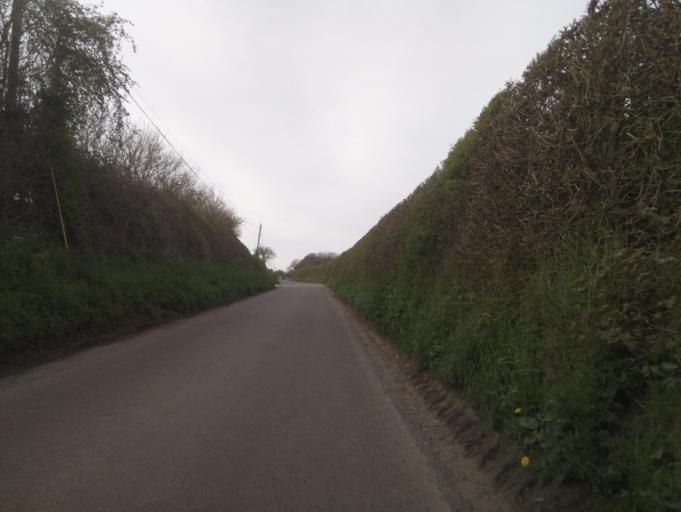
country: GB
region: England
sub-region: Somerset
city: Milborne Port
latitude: 50.9543
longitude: -2.4629
